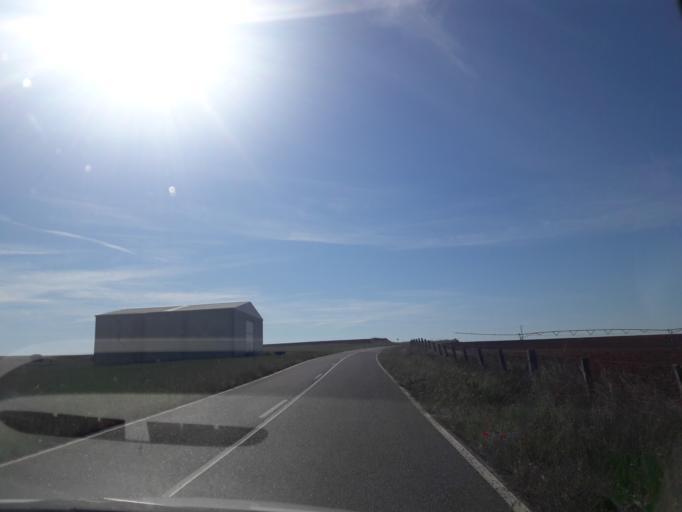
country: ES
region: Castille and Leon
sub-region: Provincia de Salamanca
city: Aldeanueva de Figueroa
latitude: 41.1476
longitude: -5.5191
